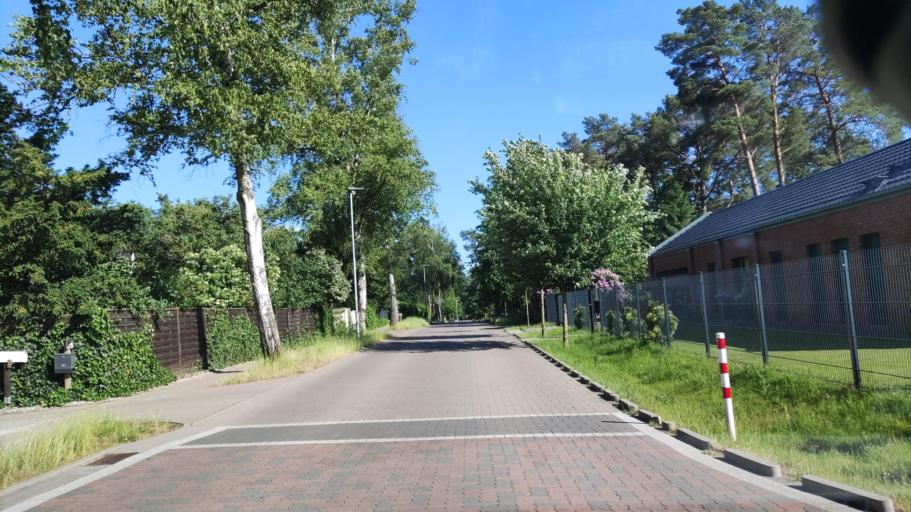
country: DE
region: Lower Saxony
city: Harmstorf
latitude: 53.3764
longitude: 10.0359
